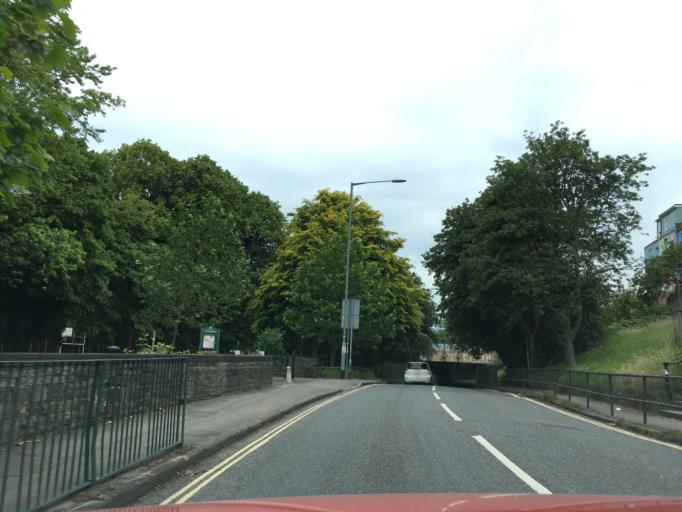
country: GB
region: England
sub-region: Bristol
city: Bristol
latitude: 51.4428
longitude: -2.5842
